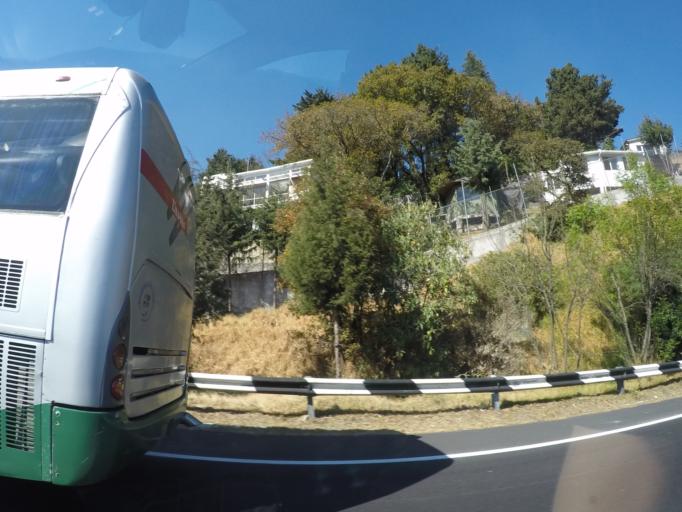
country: MX
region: Mexico City
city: Cuajimalpa
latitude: 19.3483
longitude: -99.2828
